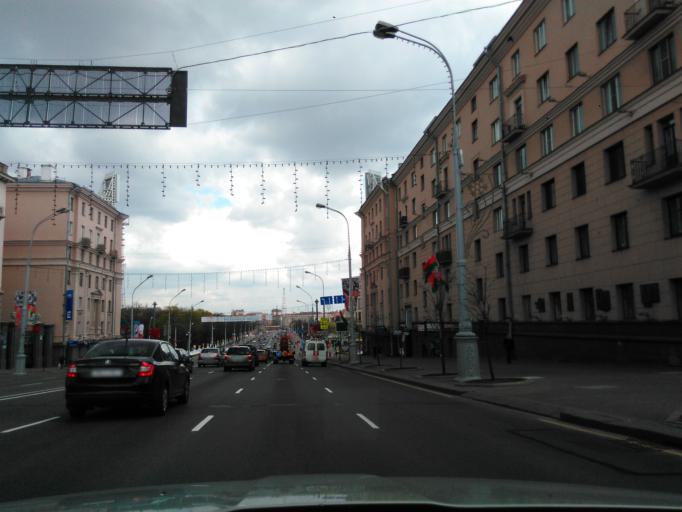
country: BY
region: Minsk
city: Minsk
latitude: 53.9033
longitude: 27.5647
